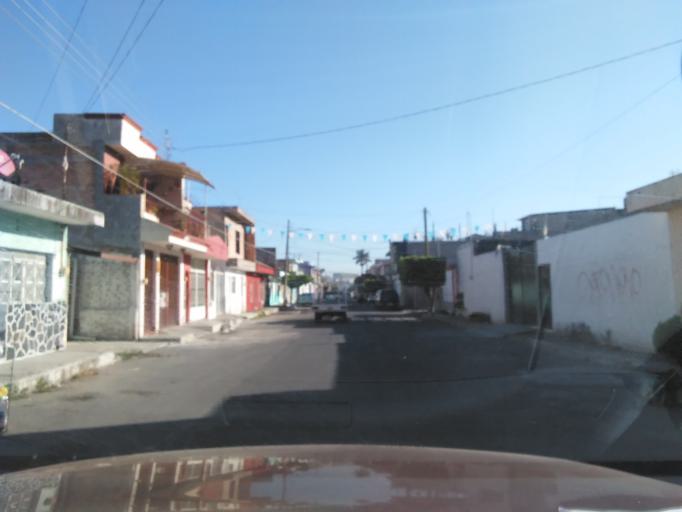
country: MX
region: Nayarit
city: Tepic
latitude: 21.5213
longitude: -104.9029
